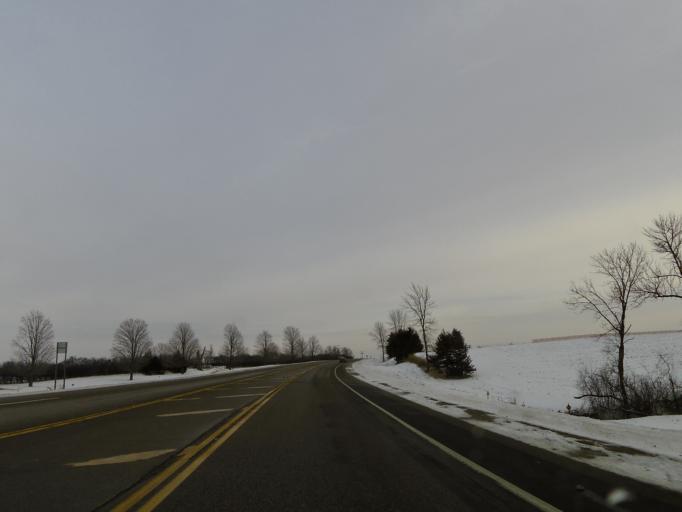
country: US
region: Minnesota
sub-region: Hennepin County
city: Saint Bonifacius
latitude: 44.8984
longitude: -93.7206
